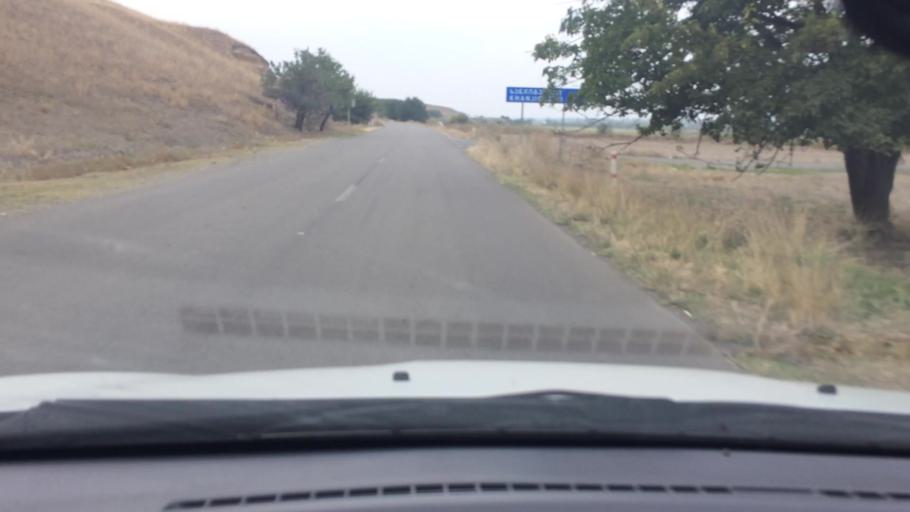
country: AM
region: Tavush
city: Berdavan
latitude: 41.3384
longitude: 45.0045
